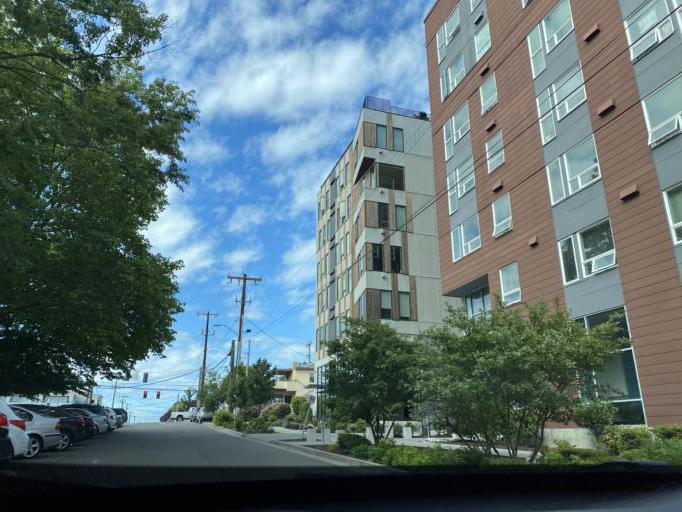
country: US
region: Washington
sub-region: King County
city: Seattle
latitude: 47.6476
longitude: -122.3788
